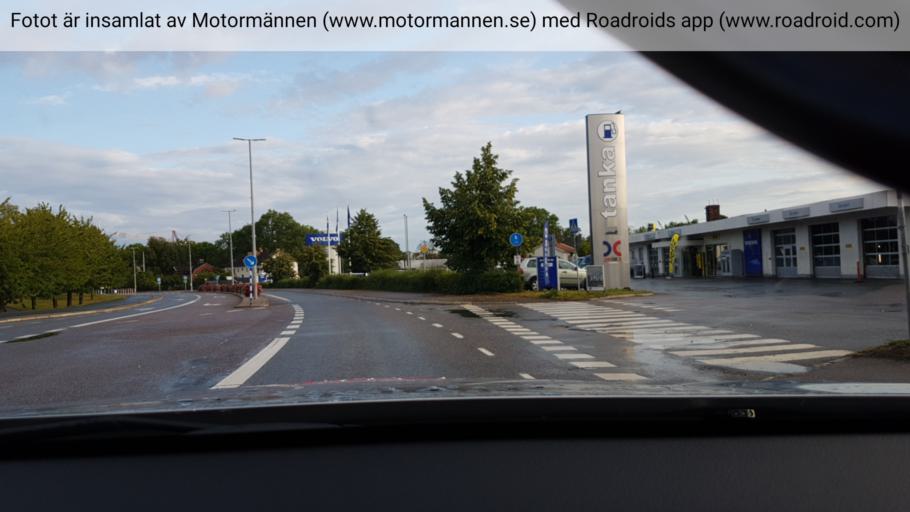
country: SE
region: Stockholm
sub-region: Norrtalje Kommun
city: Norrtalje
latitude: 59.7612
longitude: 18.6893
